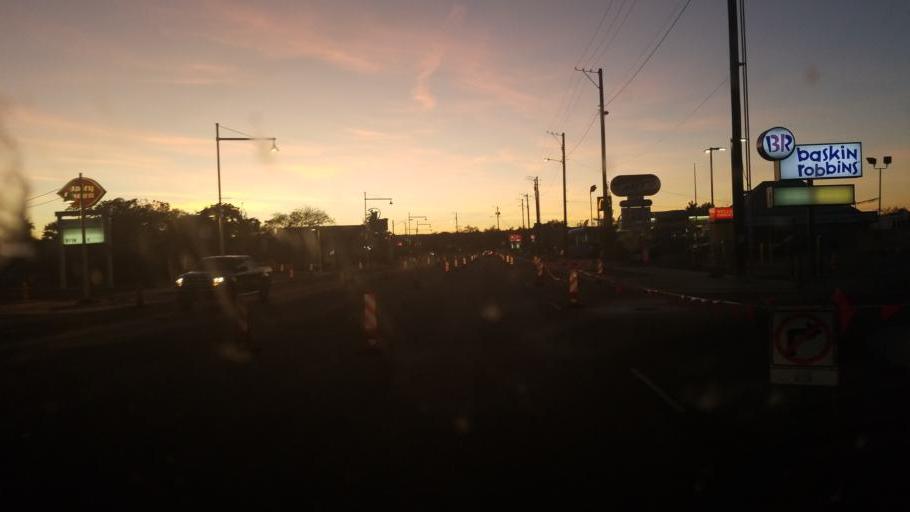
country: US
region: New Mexico
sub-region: Bernalillo County
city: Albuquerque
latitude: 35.0954
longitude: -106.6728
